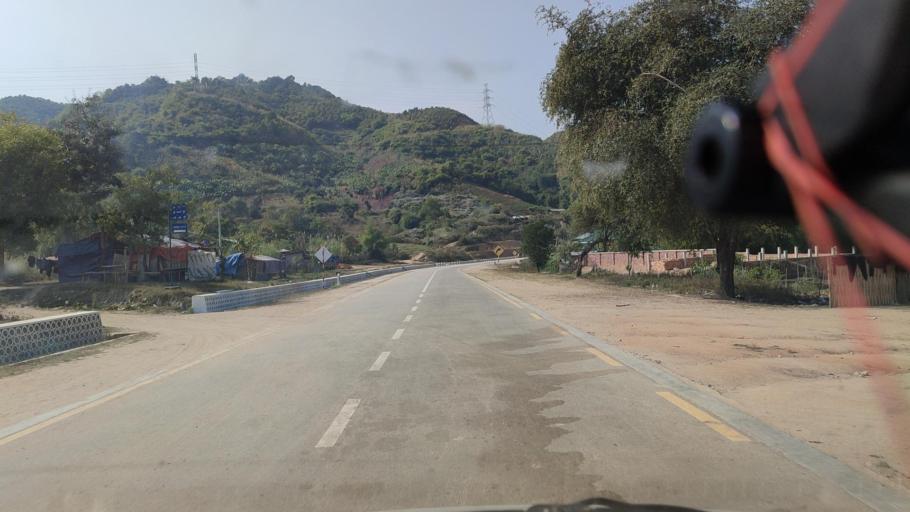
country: TH
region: Chiang Rai
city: Mae Sai
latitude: 21.2814
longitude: 99.5696
